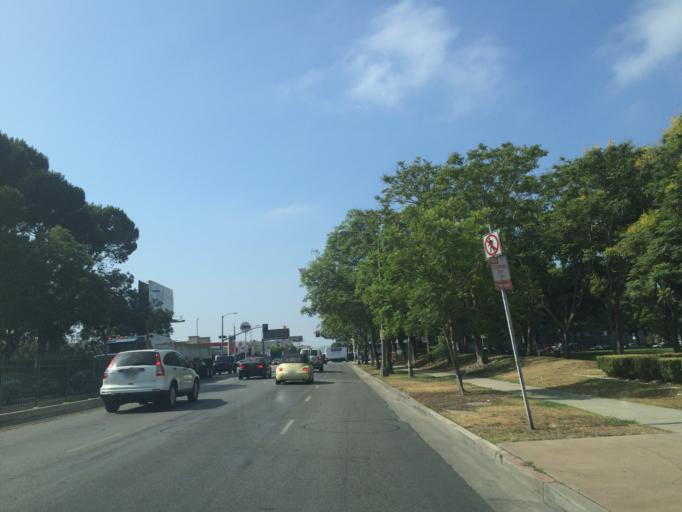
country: US
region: California
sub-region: Los Angeles County
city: Beverly Hills
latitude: 34.0607
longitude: -118.3762
